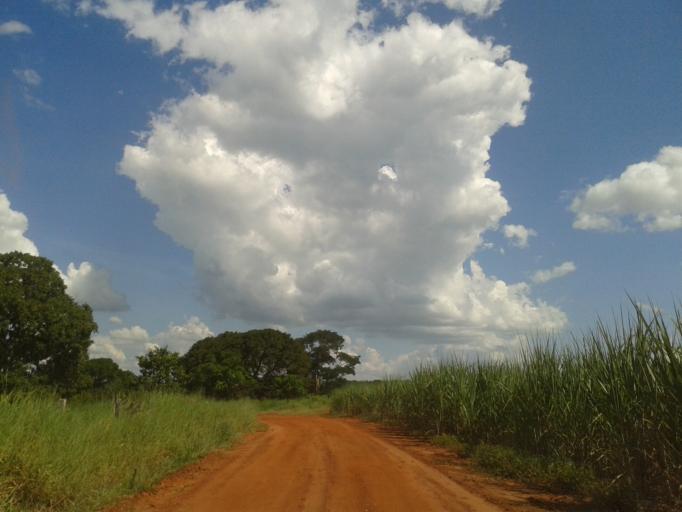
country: BR
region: Minas Gerais
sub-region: Santa Vitoria
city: Santa Vitoria
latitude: -19.1202
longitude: -50.4282
